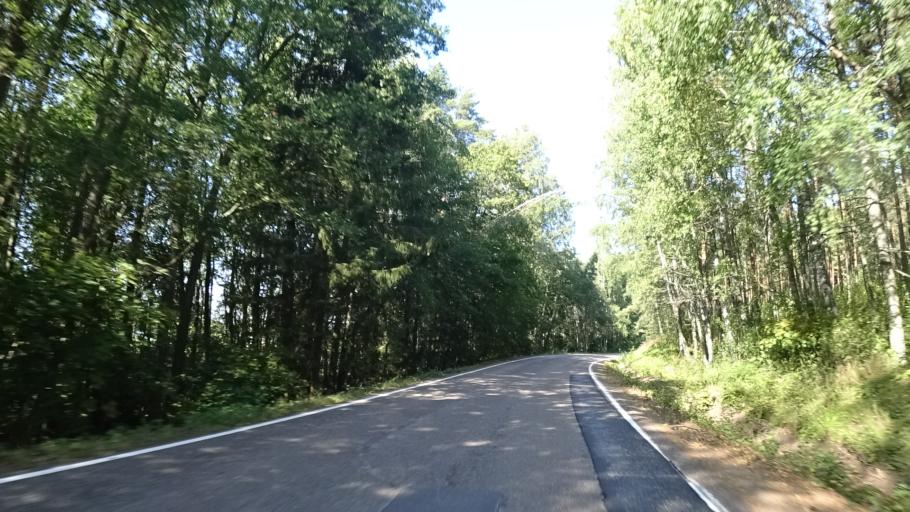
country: FI
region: Kymenlaakso
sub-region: Kotka-Hamina
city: Hamina
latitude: 60.5402
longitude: 27.2631
